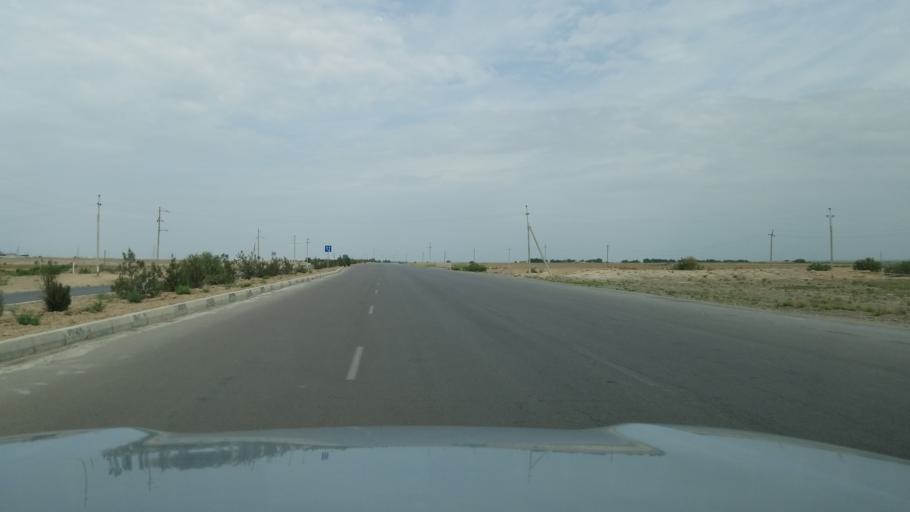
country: TM
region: Ahal
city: Arcabil
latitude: 38.2221
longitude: 57.7991
